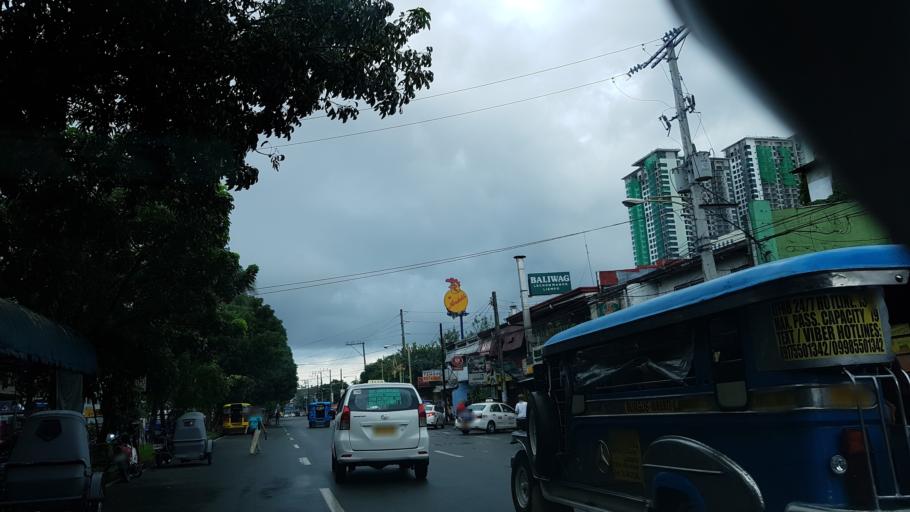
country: PH
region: Metro Manila
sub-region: Mandaluyong
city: Mandaluyong City
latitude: 14.5721
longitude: 121.0159
